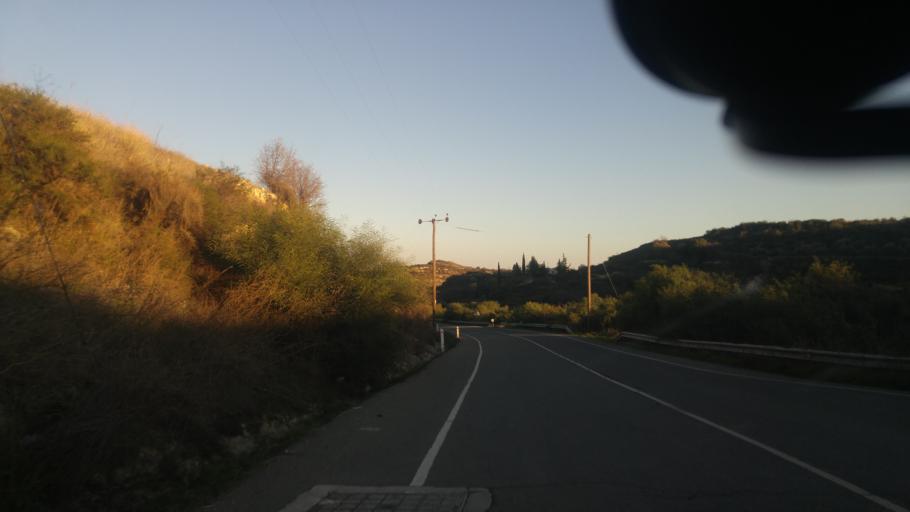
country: CY
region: Limassol
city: Pachna
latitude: 34.7960
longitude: 32.8048
